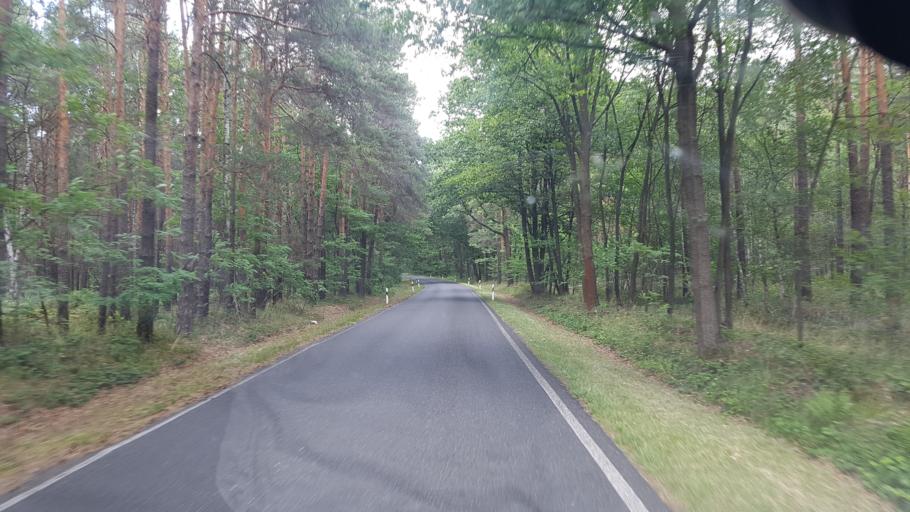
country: DE
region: Brandenburg
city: Sallgast
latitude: 51.5795
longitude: 13.9131
